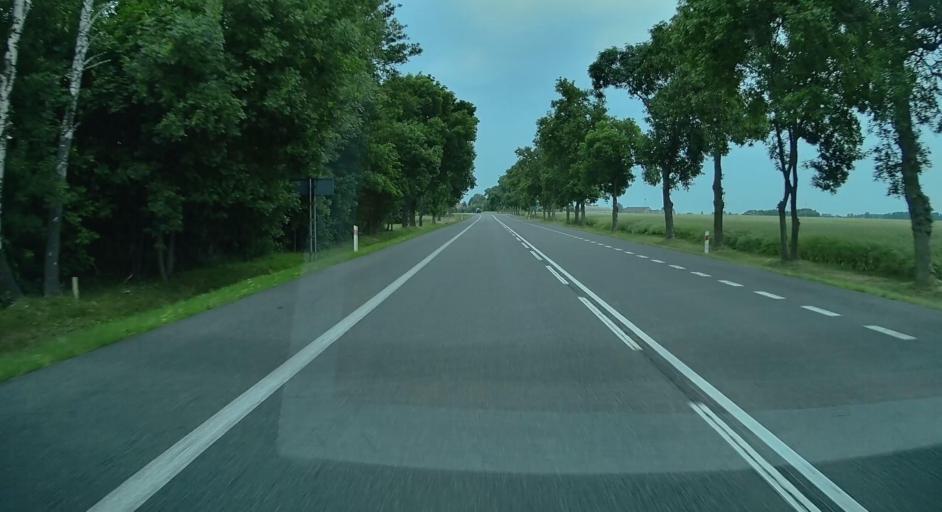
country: PL
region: Lublin Voivodeship
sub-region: Powiat lukowski
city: Trzebieszow
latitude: 52.0643
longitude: 22.5438
